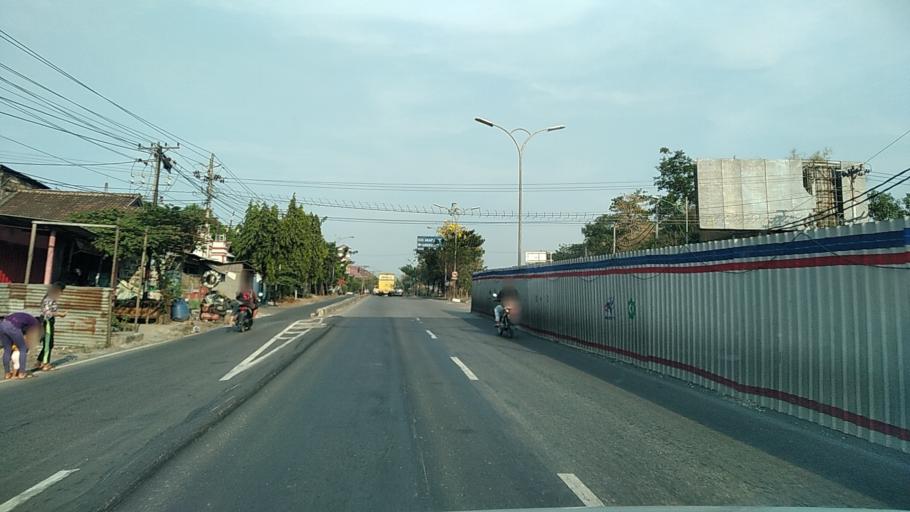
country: ID
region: Central Java
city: Semarang
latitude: -6.9685
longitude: 110.2865
